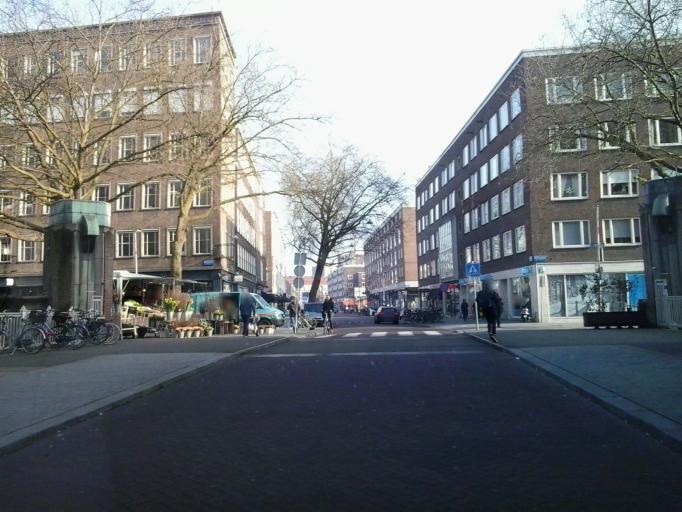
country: NL
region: South Holland
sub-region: Gemeente Rotterdam
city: Rotterdam
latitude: 51.9221
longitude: 4.4824
